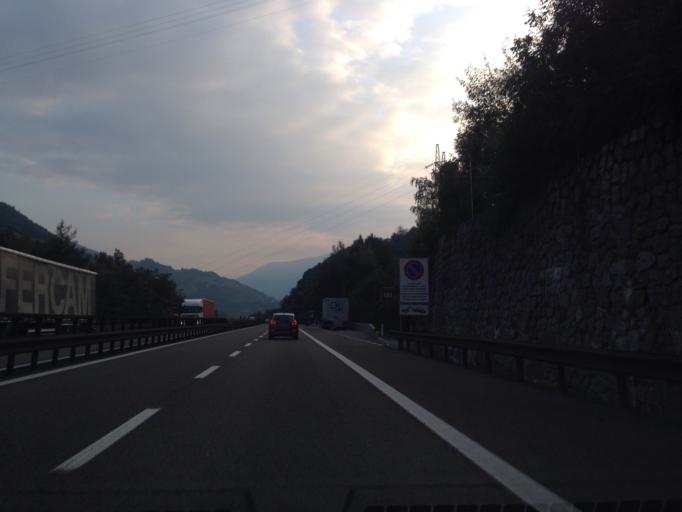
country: IT
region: Trentino-Alto Adige
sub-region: Bolzano
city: Chiusa
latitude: 46.6391
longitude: 11.5716
